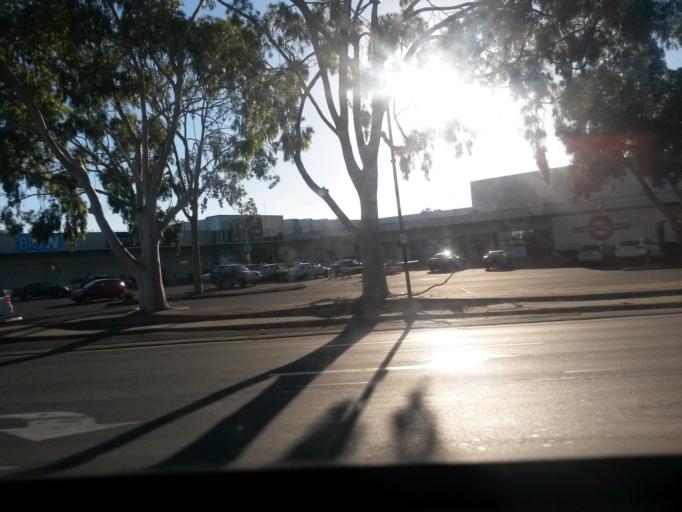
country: AU
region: South Australia
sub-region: Charles Sturt
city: Woodville North
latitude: -34.8745
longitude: 138.5483
